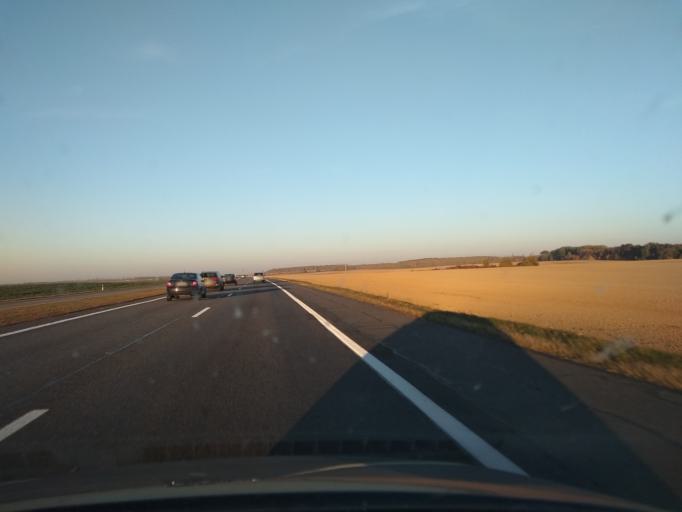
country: BY
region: Brest
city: Baranovichi
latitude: 53.2205
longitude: 26.1513
